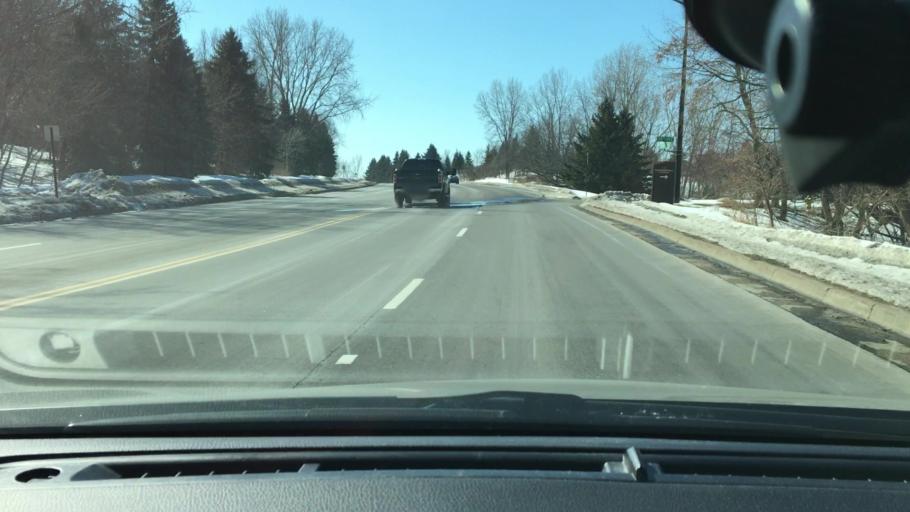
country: US
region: Minnesota
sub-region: Hennepin County
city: Maple Grove
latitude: 45.0583
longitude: -93.4451
